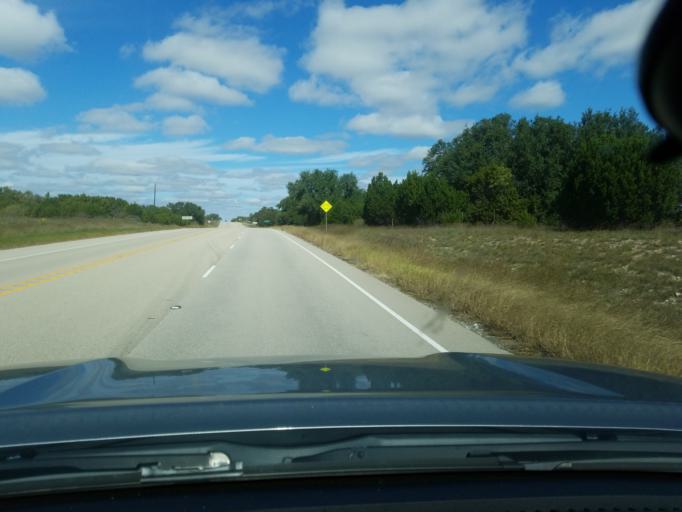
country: US
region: Texas
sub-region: Hamilton County
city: Hamilton
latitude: 31.5887
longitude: -98.1567
